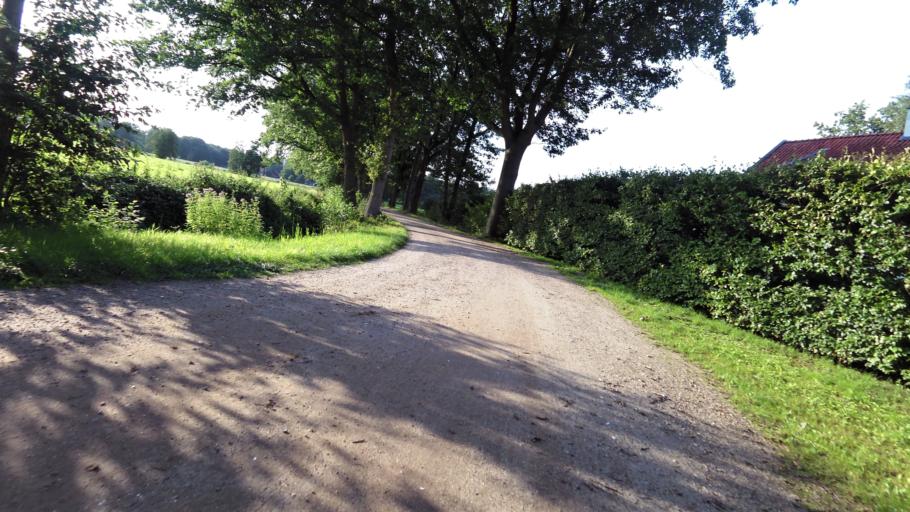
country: NL
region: Utrecht
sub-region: Gemeente Soest
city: Soest
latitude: 52.1688
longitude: 5.2549
